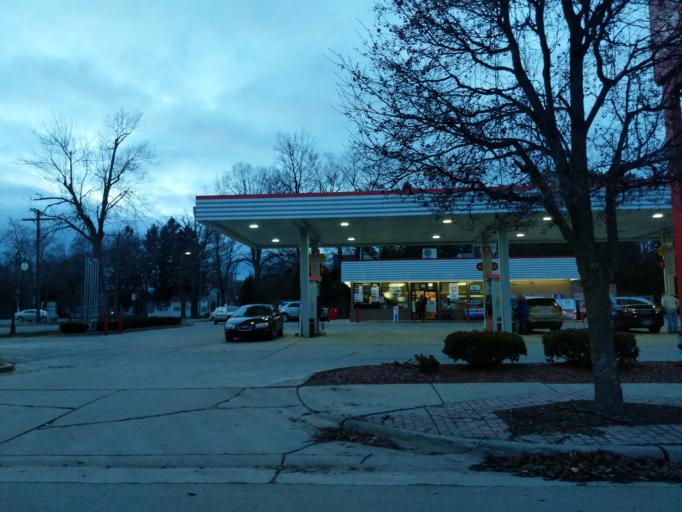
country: US
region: Michigan
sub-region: Lapeer County
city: Almont
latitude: 42.9208
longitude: -83.0452
